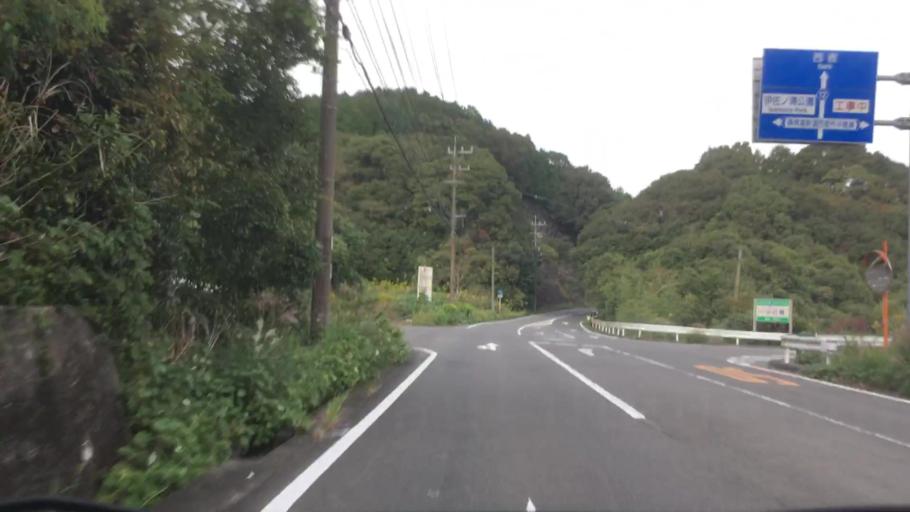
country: JP
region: Nagasaki
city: Sasebo
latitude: 32.9615
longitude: 129.6851
